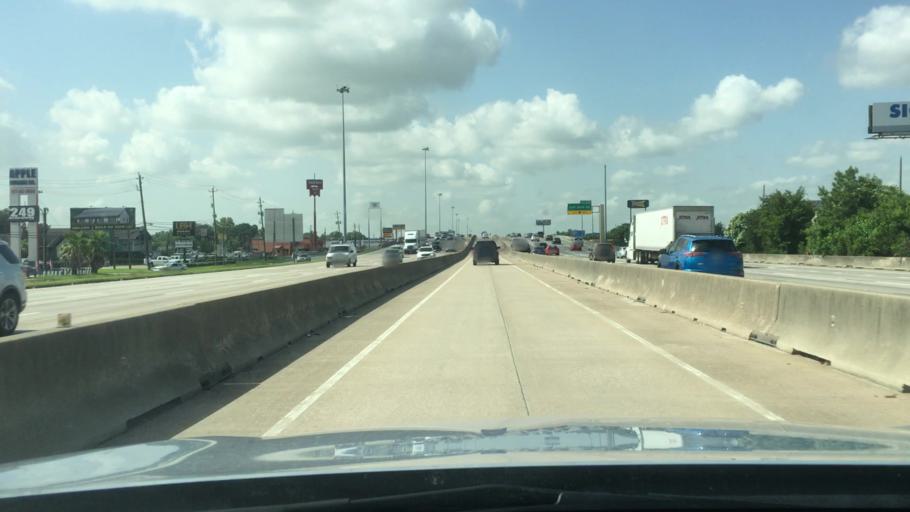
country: US
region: Texas
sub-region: Harris County
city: Aldine
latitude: 29.9016
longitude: -95.4123
